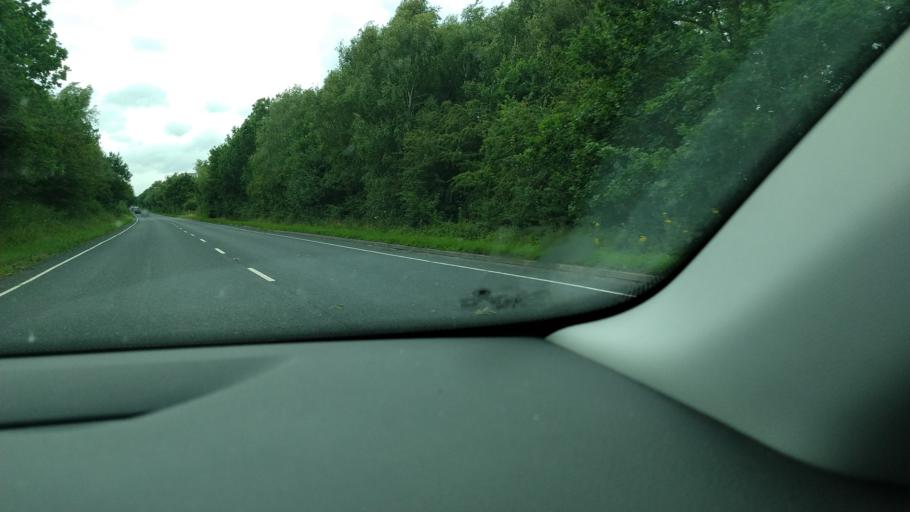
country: GB
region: England
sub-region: East Riding of Yorkshire
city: Barmby on the Marsh
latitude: 53.7164
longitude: -0.9638
